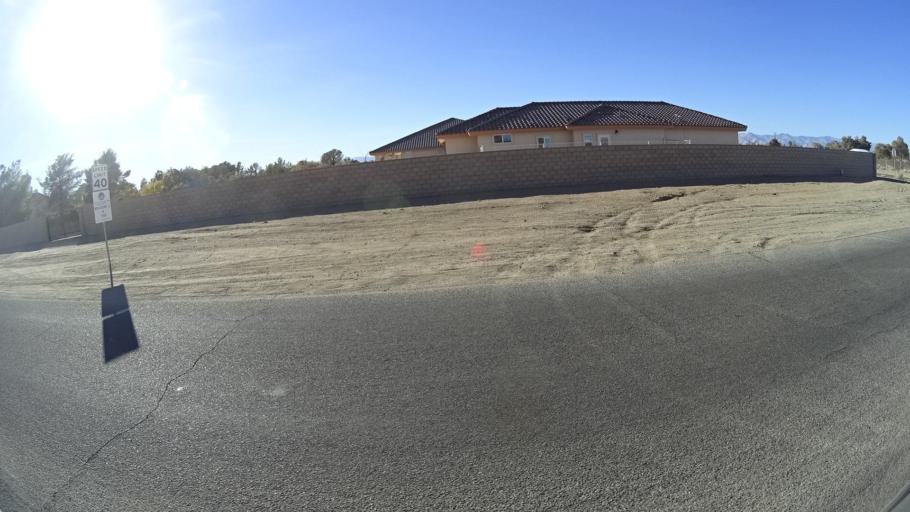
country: US
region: California
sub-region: Kern County
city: Ridgecrest
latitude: 35.6432
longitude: -117.6959
